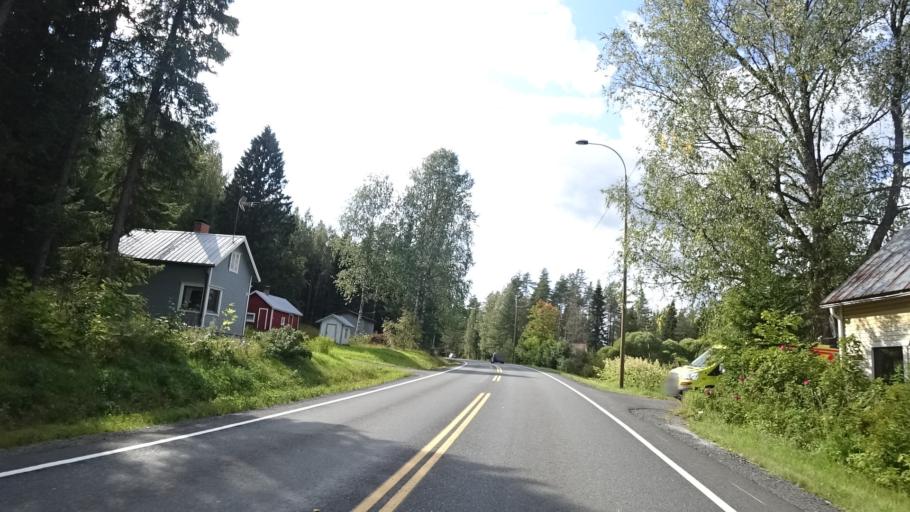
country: FI
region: North Karelia
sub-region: Keski-Karjala
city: Tohmajaervi
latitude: 62.1899
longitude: 30.4549
